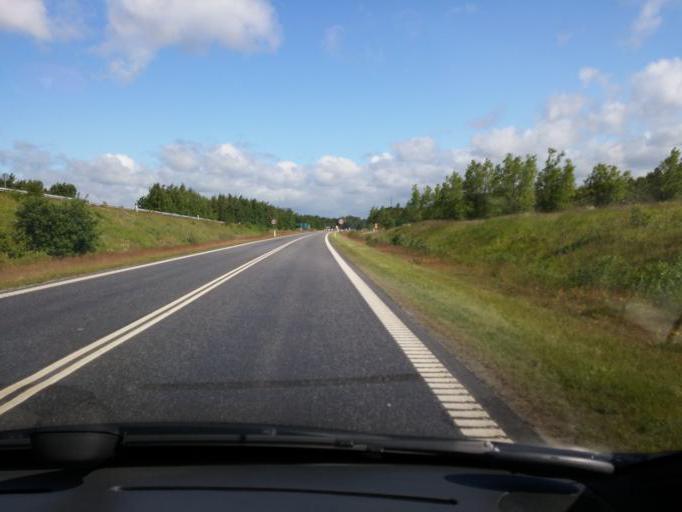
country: DK
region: Capital Region
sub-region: Hillerod Kommune
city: Hillerod
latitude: 55.9361
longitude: 12.2475
